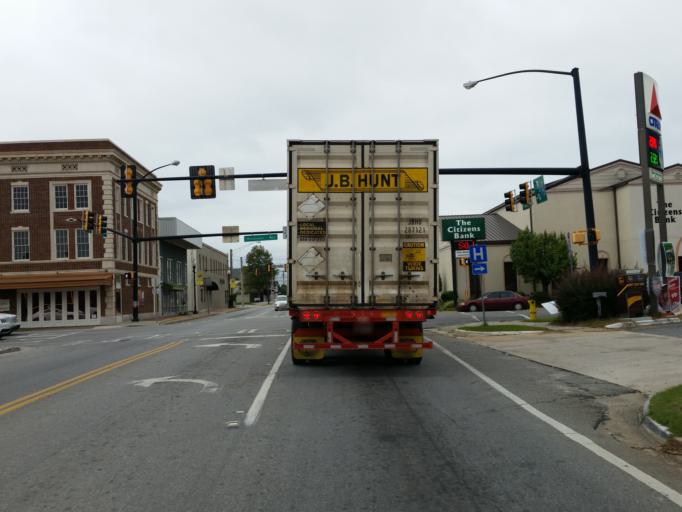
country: US
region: Georgia
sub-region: Cook County
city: Adel
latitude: 31.1372
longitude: -83.4230
